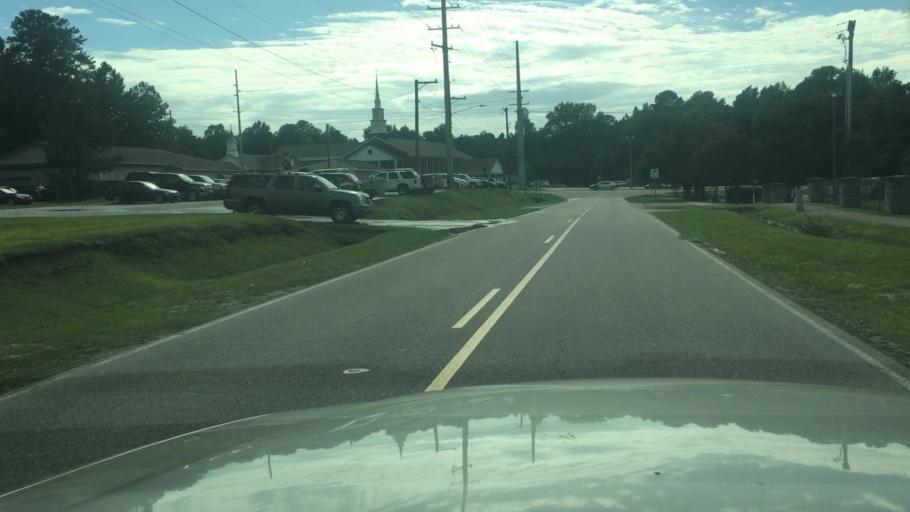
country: US
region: North Carolina
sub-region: Cumberland County
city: Eastover
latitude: 35.1502
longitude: -78.8692
